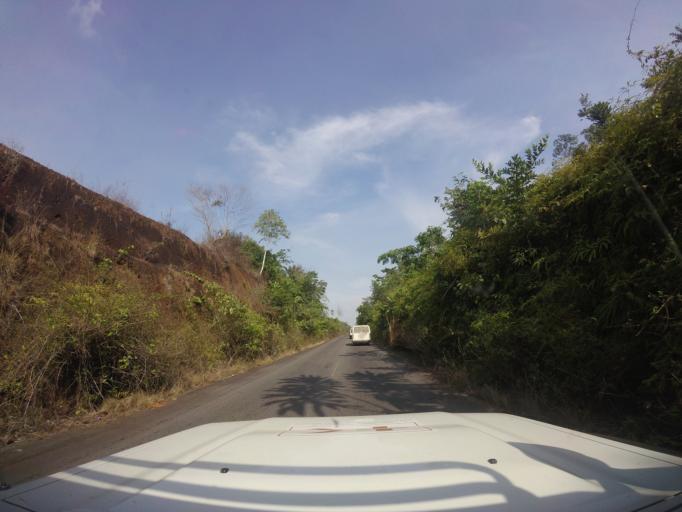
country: LR
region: Bomi
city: Tubmanburg
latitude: 6.6941
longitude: -10.8974
